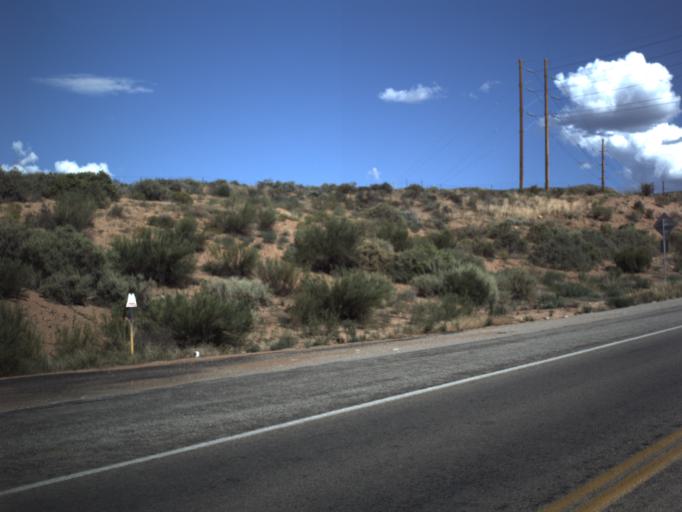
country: US
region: Utah
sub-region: Washington County
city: LaVerkin
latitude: 37.2190
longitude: -113.2755
